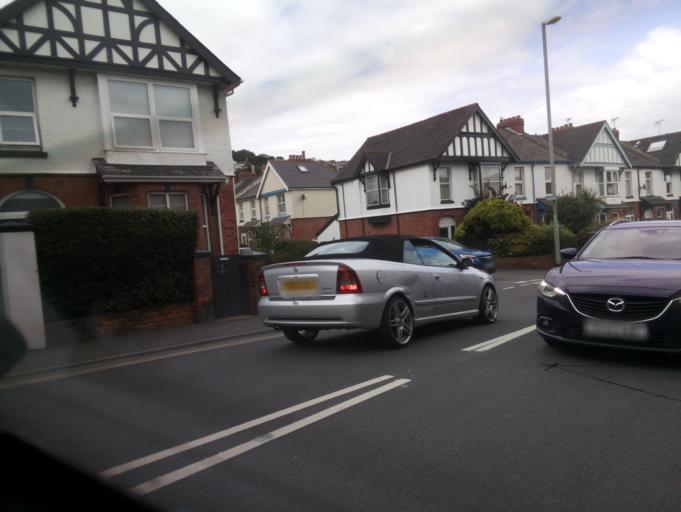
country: GB
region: England
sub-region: Devon
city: Teignmouth
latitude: 50.5478
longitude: -3.5084
